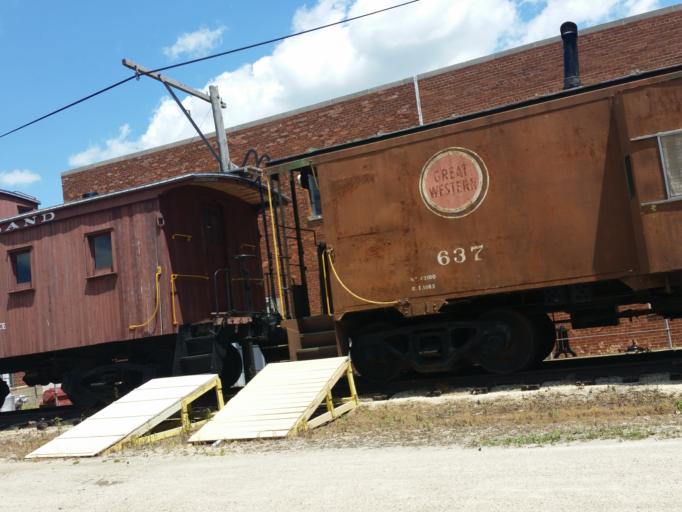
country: US
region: Iowa
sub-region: Fayette County
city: Oelwein
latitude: 42.6771
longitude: -91.9167
